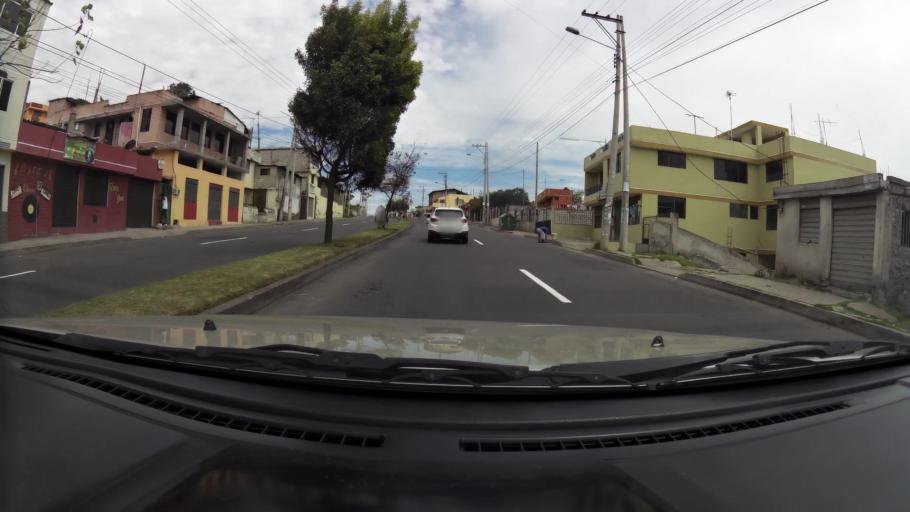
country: EC
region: Tungurahua
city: Pillaro
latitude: -1.1248
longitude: -78.5889
